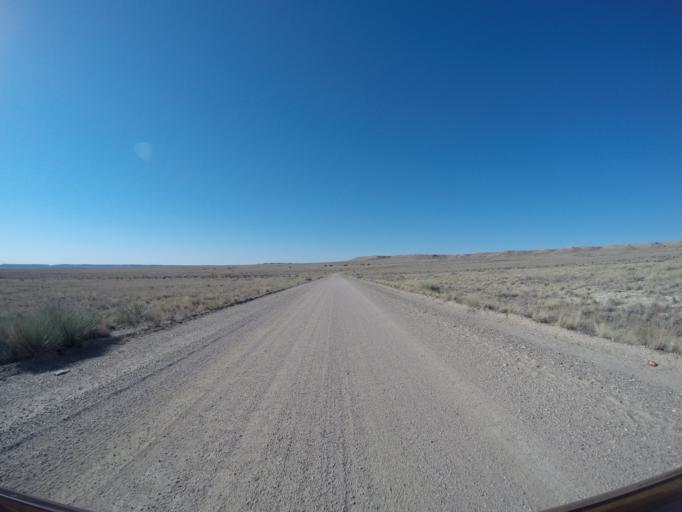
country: US
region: Colorado
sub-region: Otero County
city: La Junta
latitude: 37.7472
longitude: -103.6178
